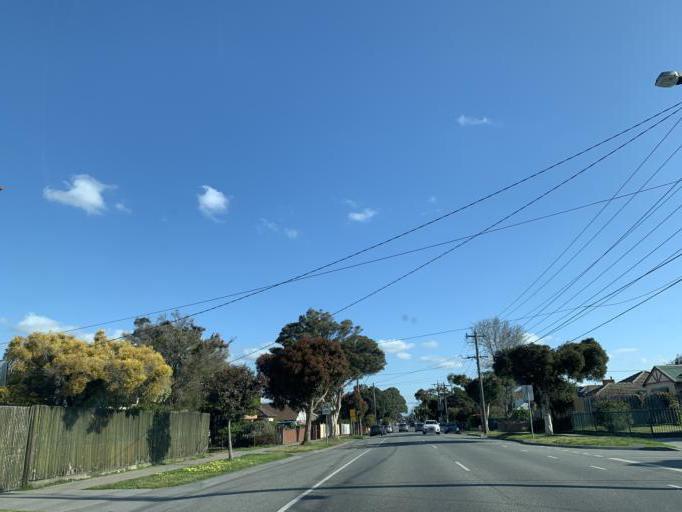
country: AU
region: Victoria
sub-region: Kingston
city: Mordialloc
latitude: -37.9875
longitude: 145.0938
